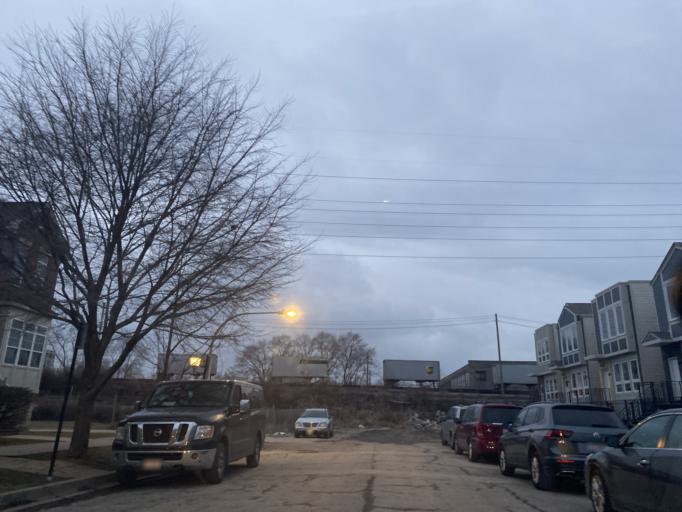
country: US
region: Illinois
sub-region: Cook County
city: Chicago
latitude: 41.8675
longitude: -87.6901
